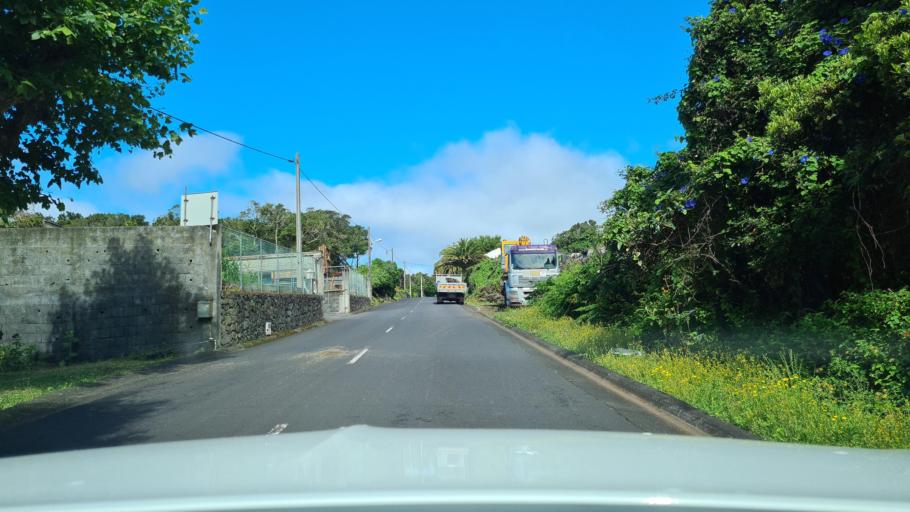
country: PT
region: Azores
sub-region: Sao Roque do Pico
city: Sao Roque do Pico
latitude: 38.6404
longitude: -28.1152
